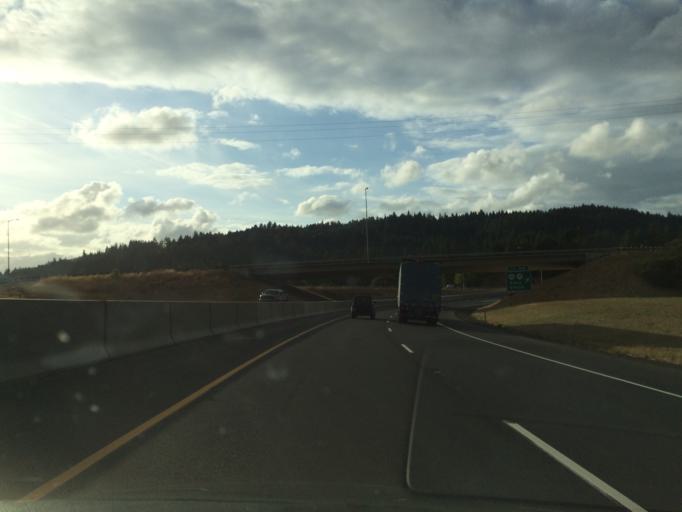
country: US
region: Oregon
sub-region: Douglas County
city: Drain
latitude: 43.7077
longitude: -123.2161
